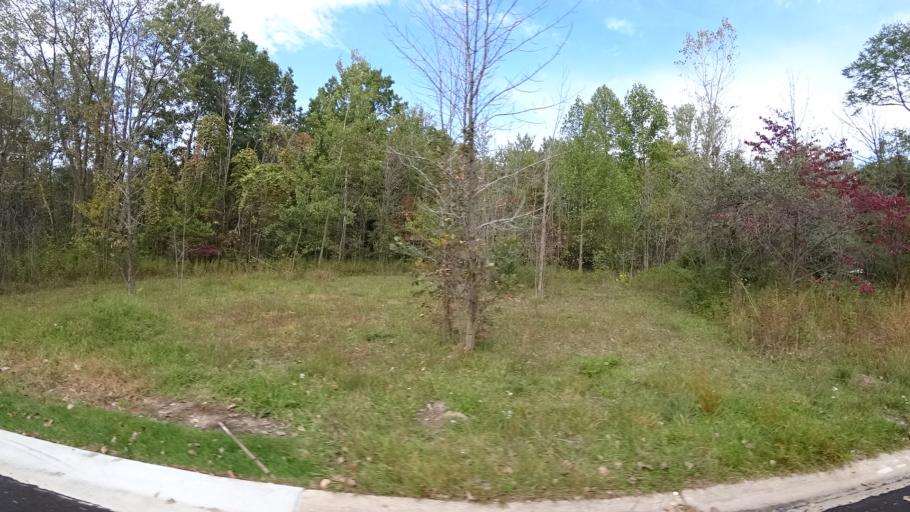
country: US
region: Indiana
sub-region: LaPorte County
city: Trail Creek
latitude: 41.7170
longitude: -86.8379
